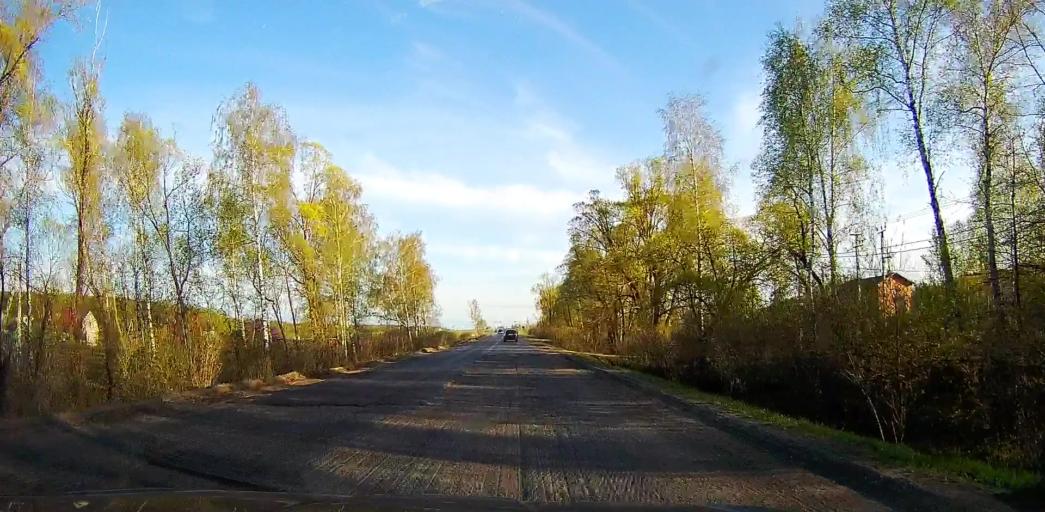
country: RU
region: Moskovskaya
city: Bronnitsy
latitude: 55.3009
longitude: 38.2104
